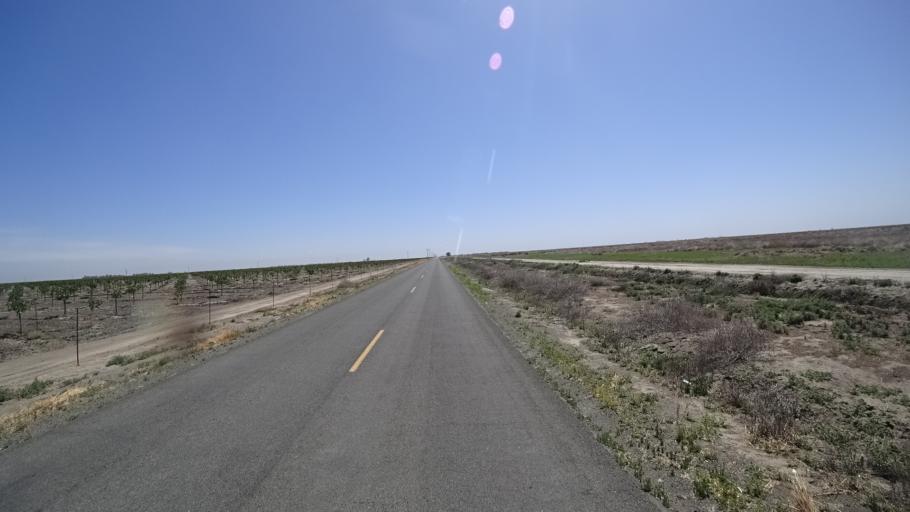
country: US
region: California
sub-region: Kings County
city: Stratford
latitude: 36.1893
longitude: -119.7313
